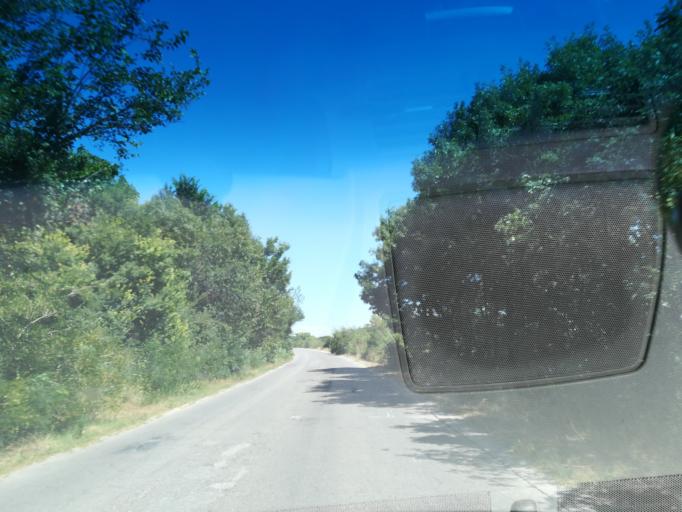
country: BG
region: Plovdiv
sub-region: Obshtina Sadovo
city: Sadovo
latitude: 42.0245
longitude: 24.9943
